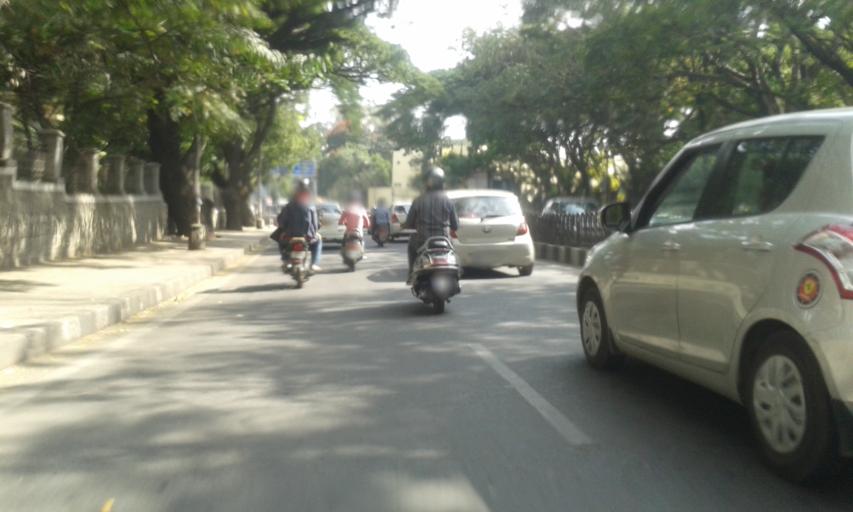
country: IN
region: Karnataka
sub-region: Bangalore Urban
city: Bangalore
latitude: 12.9393
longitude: 77.5981
